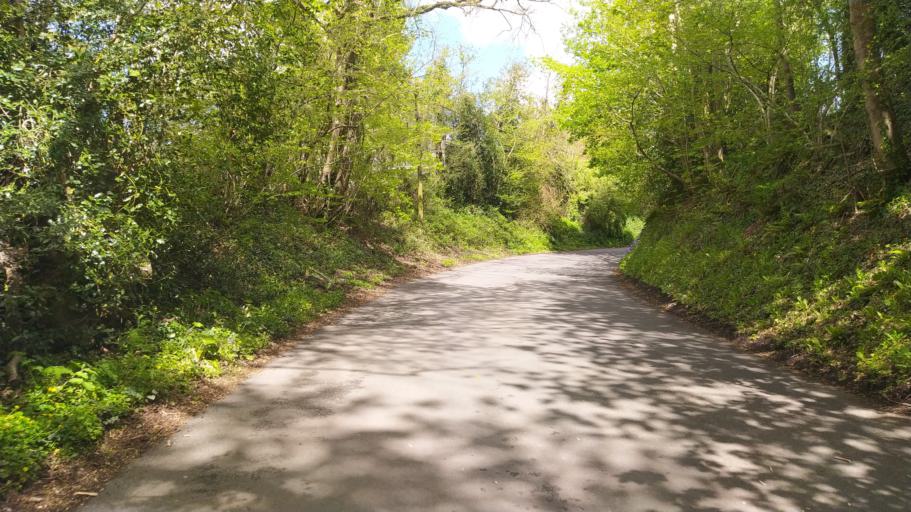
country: GB
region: England
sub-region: Wiltshire
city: Warminster
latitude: 51.1818
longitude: -2.1962
